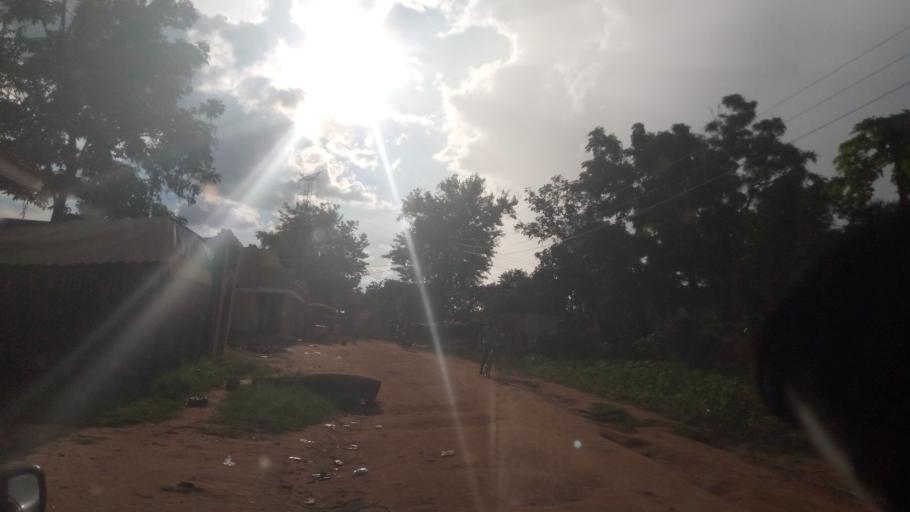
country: UG
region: Northern Region
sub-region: Lira District
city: Lira
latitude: 2.2280
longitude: 32.8942
